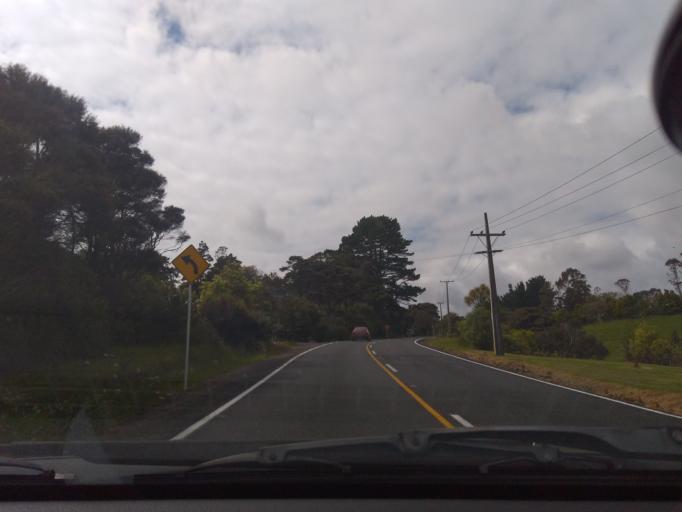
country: NZ
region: Auckland
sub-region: Auckland
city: Muriwai Beach
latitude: -36.8599
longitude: 174.5541
